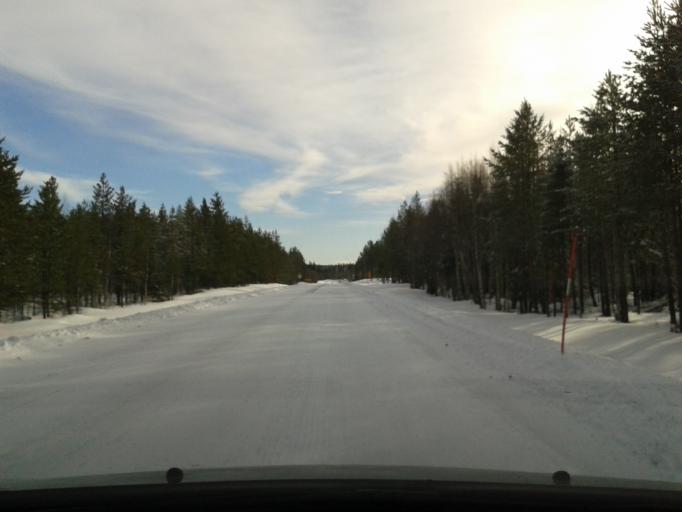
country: SE
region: Vaesterbotten
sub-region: Vilhelmina Kommun
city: Vilhelmina
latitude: 64.5284
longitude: 16.7584
